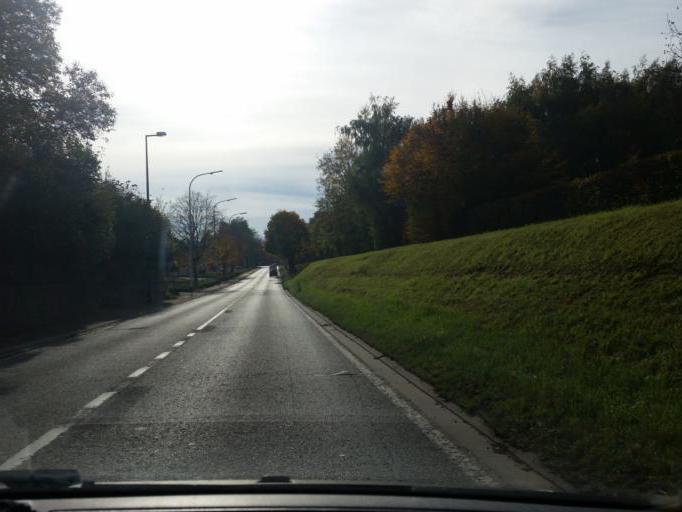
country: BE
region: Flanders
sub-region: Provincie Vlaams-Brabant
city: Grimbergen
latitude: 50.9255
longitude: 4.3656
